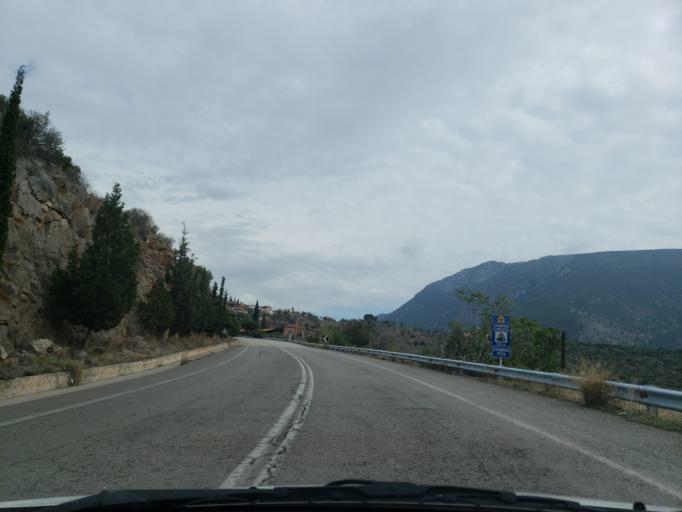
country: GR
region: Central Greece
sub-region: Nomos Fokidos
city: Delphi
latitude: 38.4714
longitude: 22.4616
